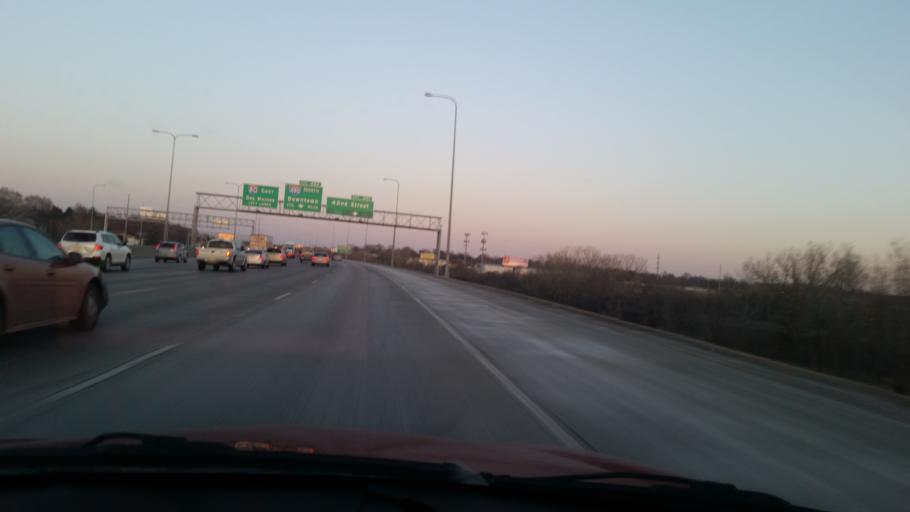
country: US
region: Nebraska
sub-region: Douglas County
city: Ralston
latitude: 41.2226
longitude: -95.9946
